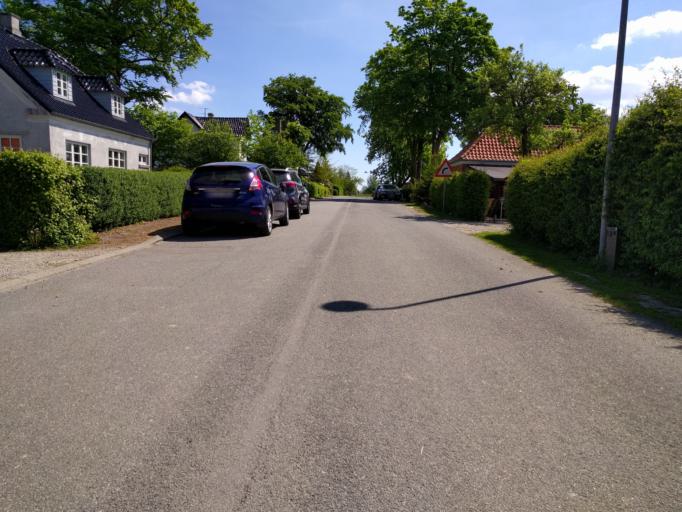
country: DK
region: Zealand
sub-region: Guldborgsund Kommune
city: Nykobing Falster
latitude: 54.7431
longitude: 11.9796
